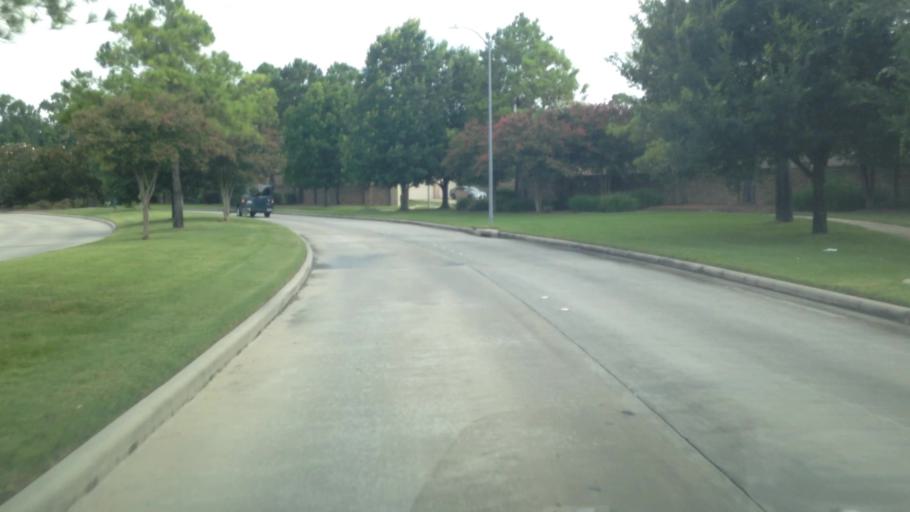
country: US
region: Texas
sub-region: Harris County
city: Atascocita
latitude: 29.9262
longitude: -95.1958
